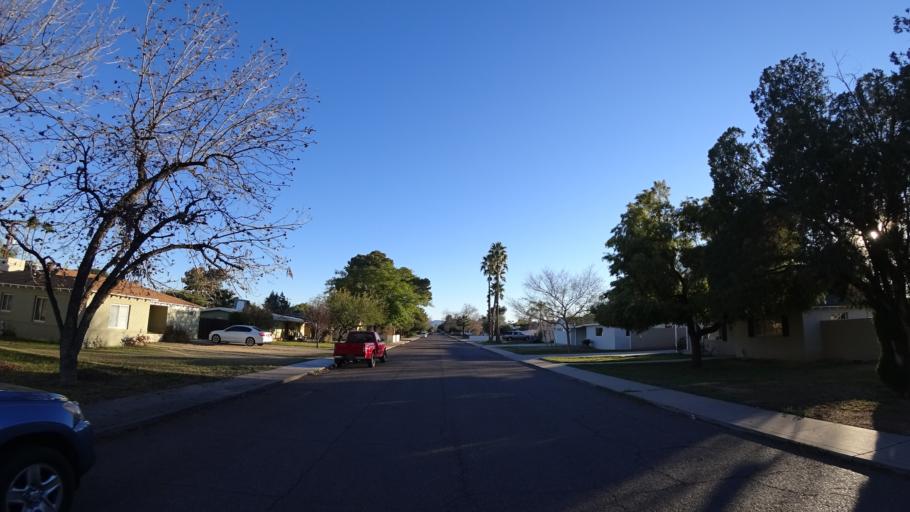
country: US
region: Arizona
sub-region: Maricopa County
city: Phoenix
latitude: 33.4862
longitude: -112.0356
